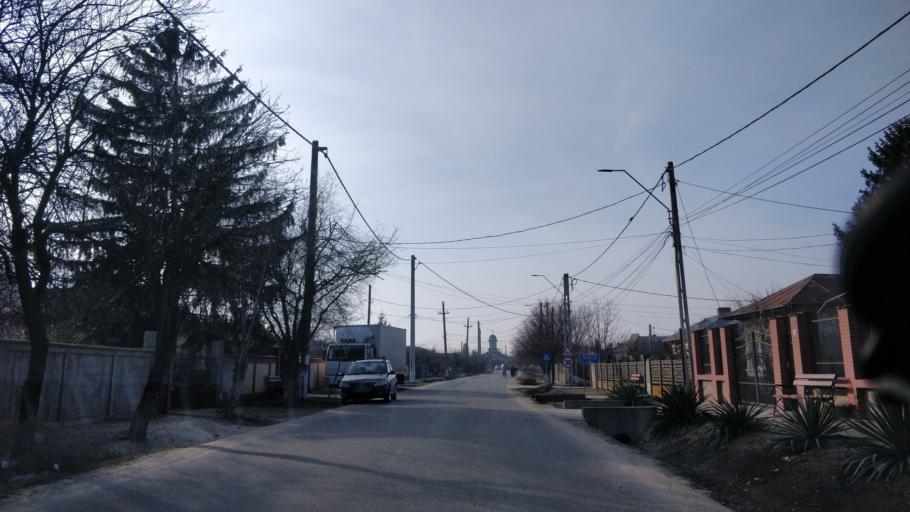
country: RO
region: Giurgiu
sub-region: Comuna Ulmi
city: Ulmi
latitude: 44.4830
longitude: 25.8019
